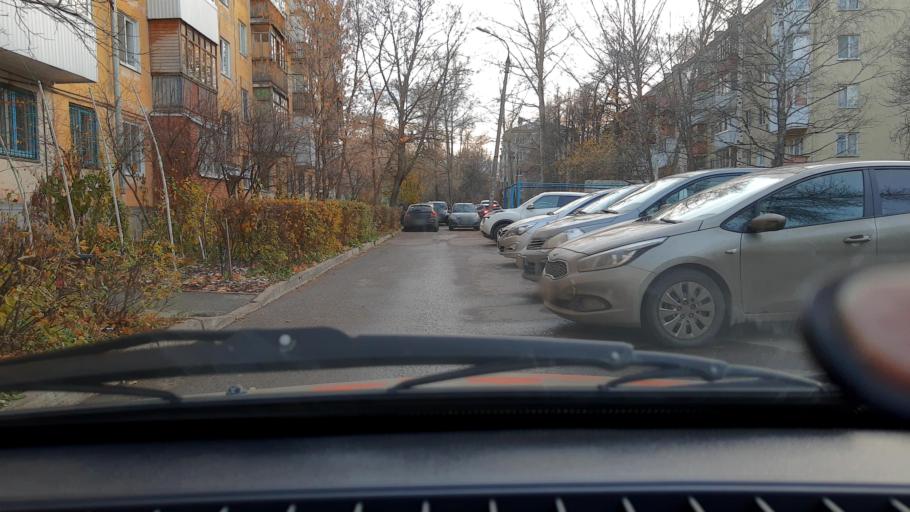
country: RU
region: Bashkortostan
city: Ufa
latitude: 54.7807
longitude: 56.0258
